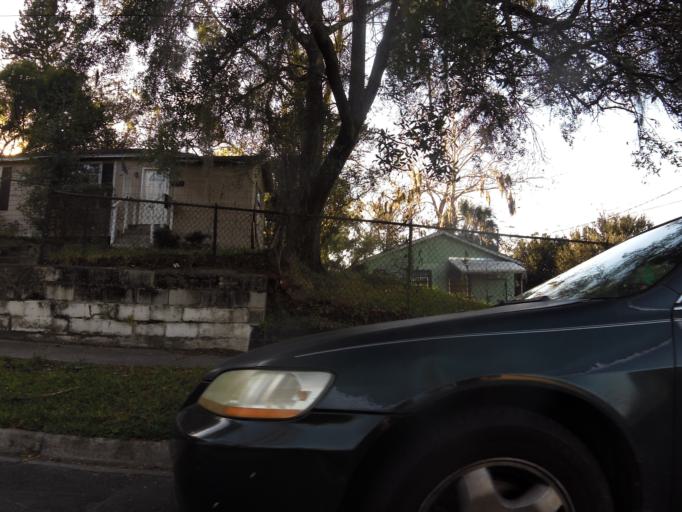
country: US
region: Florida
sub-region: Duval County
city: Jacksonville
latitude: 30.3264
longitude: -81.6968
